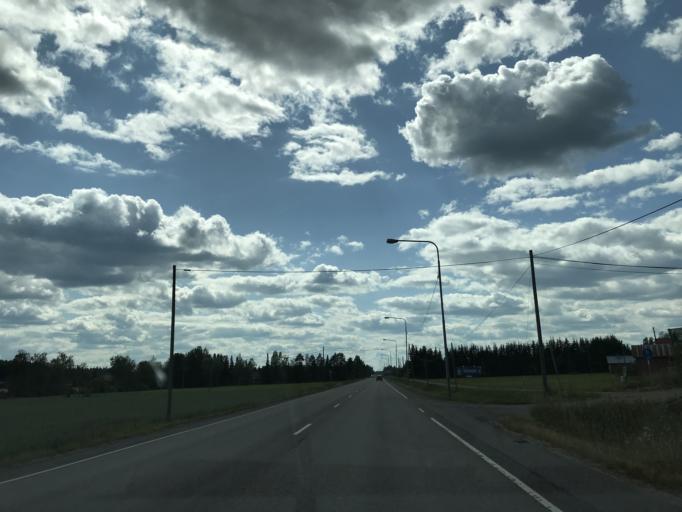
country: FI
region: Uusimaa
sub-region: Helsinki
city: Maentsaelae
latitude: 60.6499
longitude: 25.3371
